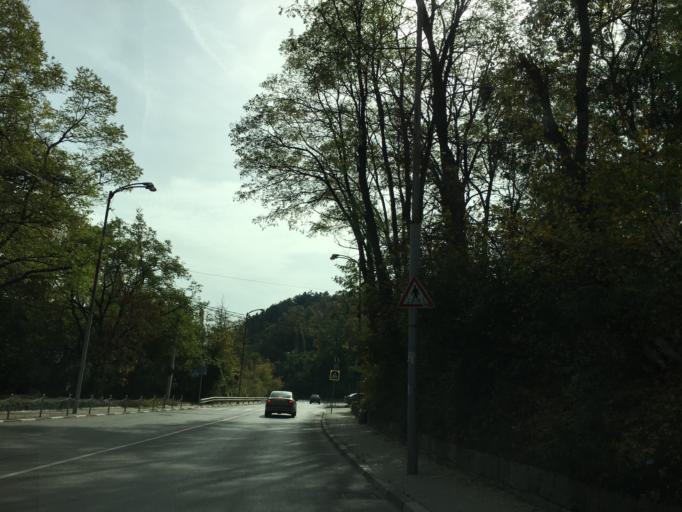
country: BG
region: Sofia-Capital
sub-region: Stolichna Obshtina
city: Sofia
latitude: 42.5949
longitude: 23.4152
